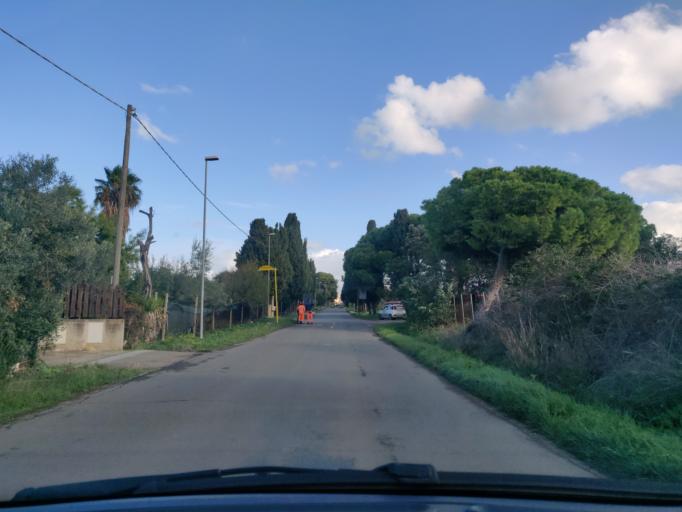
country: IT
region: Latium
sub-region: Citta metropolitana di Roma Capitale
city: Aurelia
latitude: 42.1335
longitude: 11.7881
